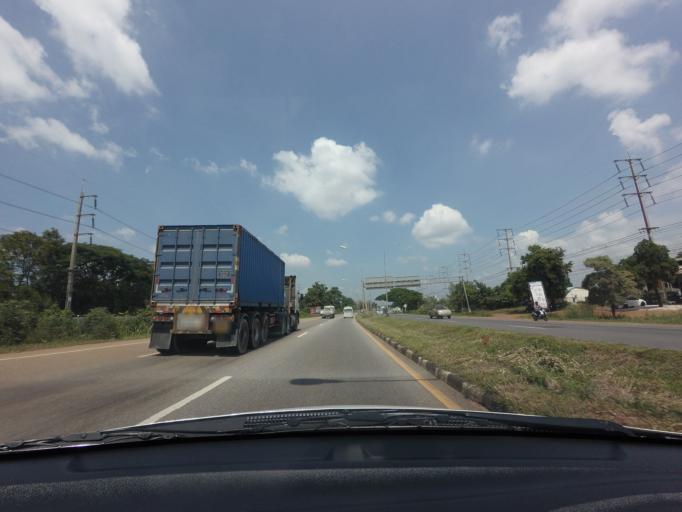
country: TH
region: Prachin Buri
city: Si Maha Phot
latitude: 13.8632
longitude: 101.5554
